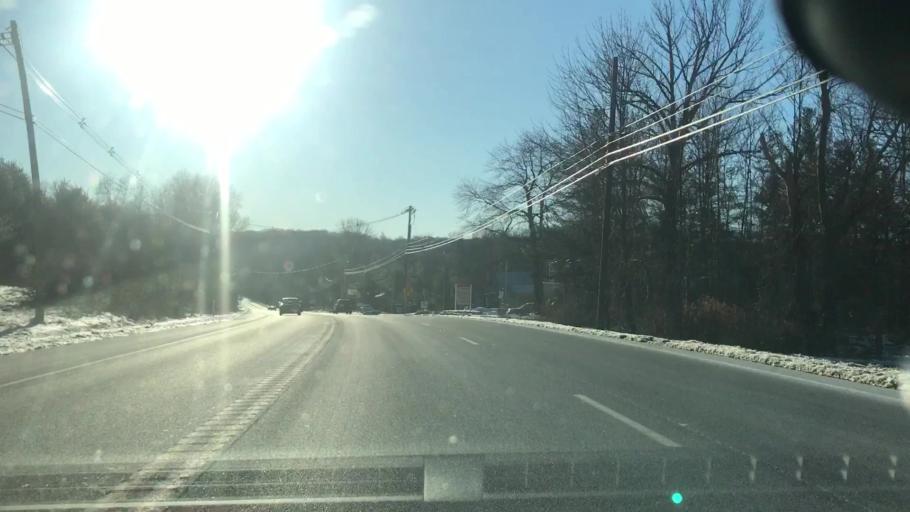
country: US
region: New Jersey
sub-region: Morris County
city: Chester
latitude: 40.8021
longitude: -74.7135
